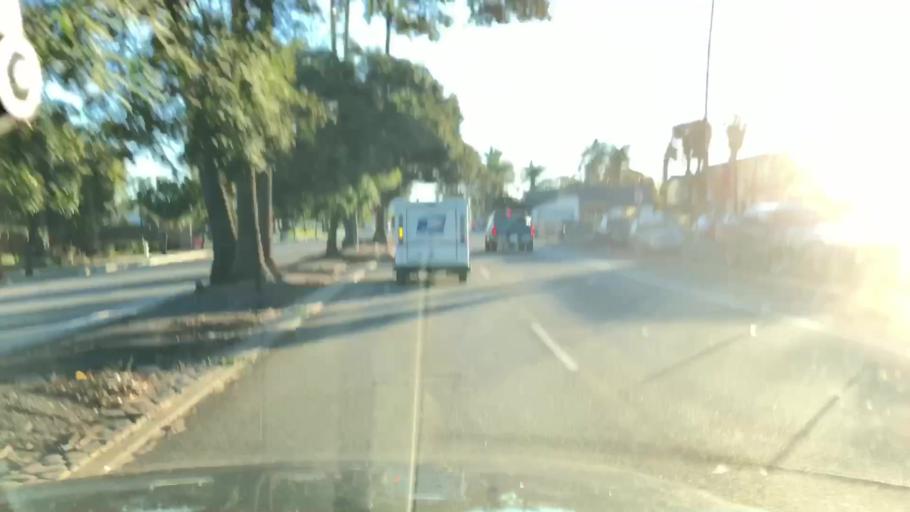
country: US
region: California
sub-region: Ventura County
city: Oxnard
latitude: 34.2191
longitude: -119.1828
